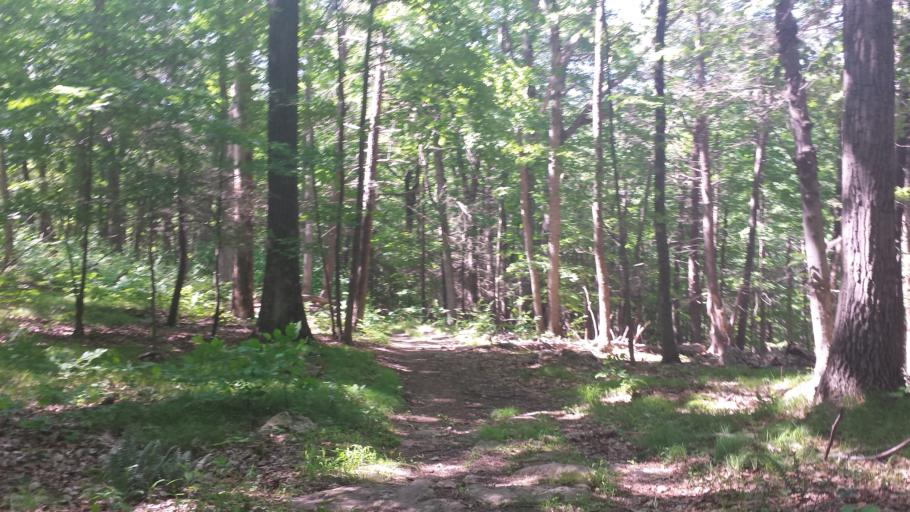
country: US
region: New York
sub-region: Westchester County
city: Pound Ridge
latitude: 41.2407
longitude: -73.5922
